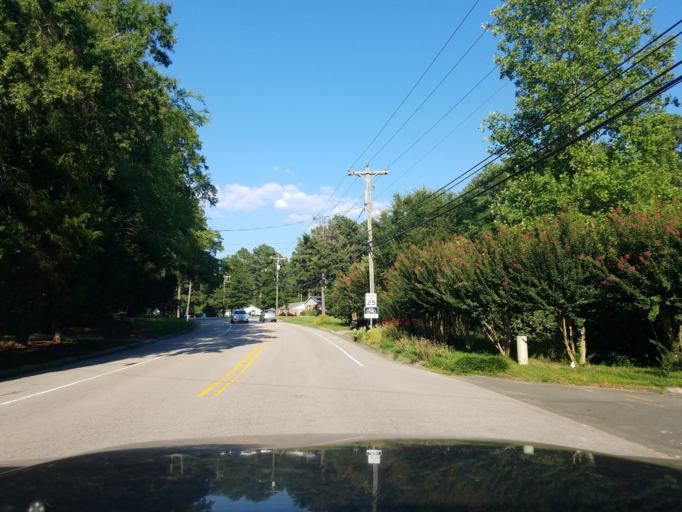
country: US
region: North Carolina
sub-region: Wake County
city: Green Level
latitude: 35.8825
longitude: -78.9118
